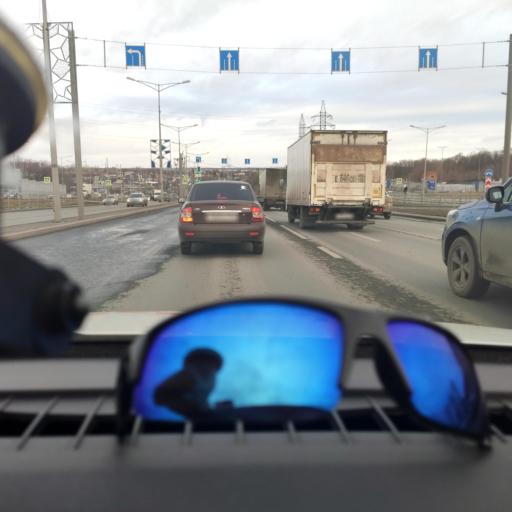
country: RU
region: Samara
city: Petra-Dubrava
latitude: 53.2796
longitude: 50.2710
